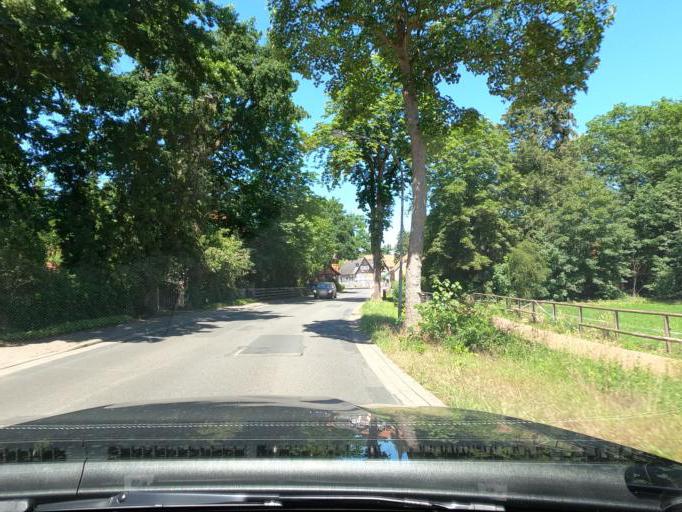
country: DE
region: Lower Saxony
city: Wienhausen
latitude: 52.5785
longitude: 10.1854
